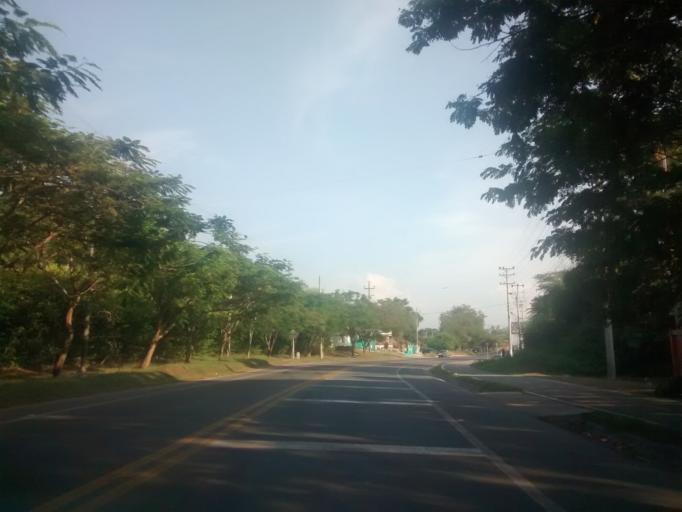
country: CO
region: Cundinamarca
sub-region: Girardot
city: Girardot City
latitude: 4.2984
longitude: -74.7911
